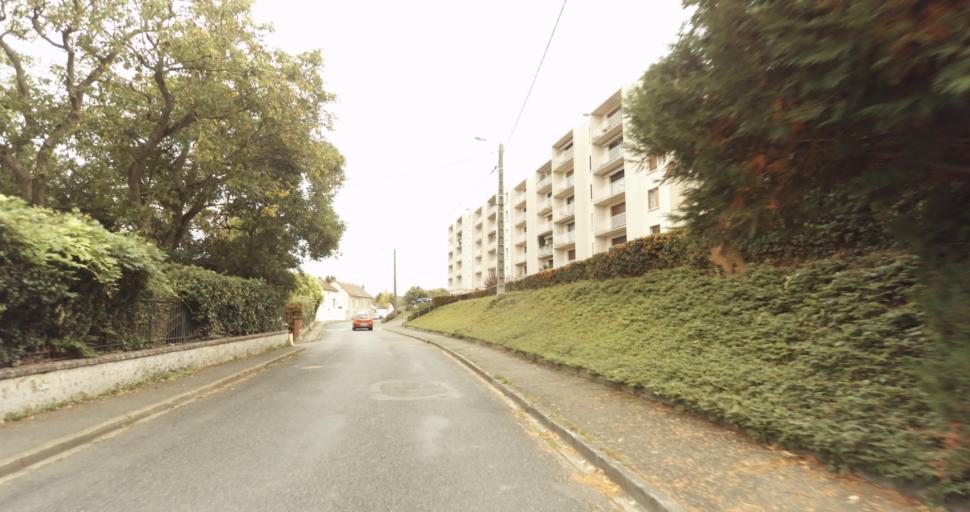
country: FR
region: Centre
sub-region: Departement d'Eure-et-Loir
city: Vernouillet
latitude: 48.7224
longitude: 1.3587
